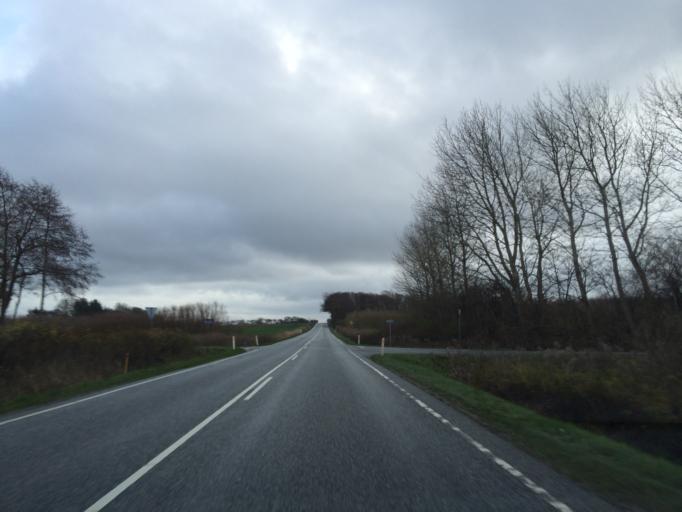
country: DK
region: Central Jutland
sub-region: Ringkobing-Skjern Kommune
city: Skjern
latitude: 56.0403
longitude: 8.4062
